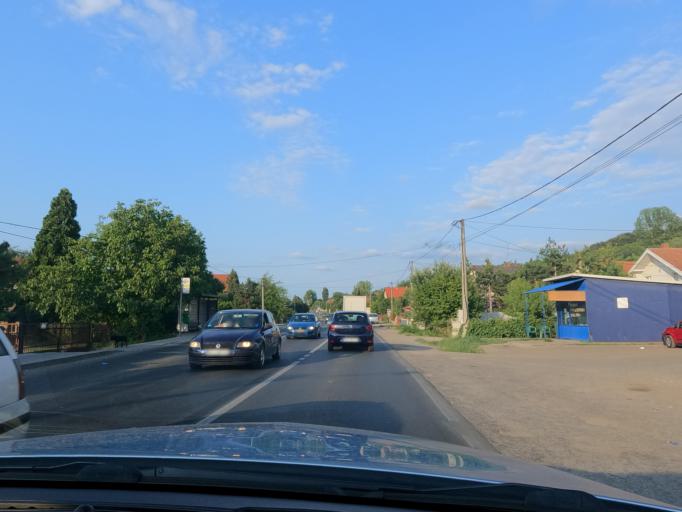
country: RS
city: Baric
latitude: 44.6526
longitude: 20.2609
